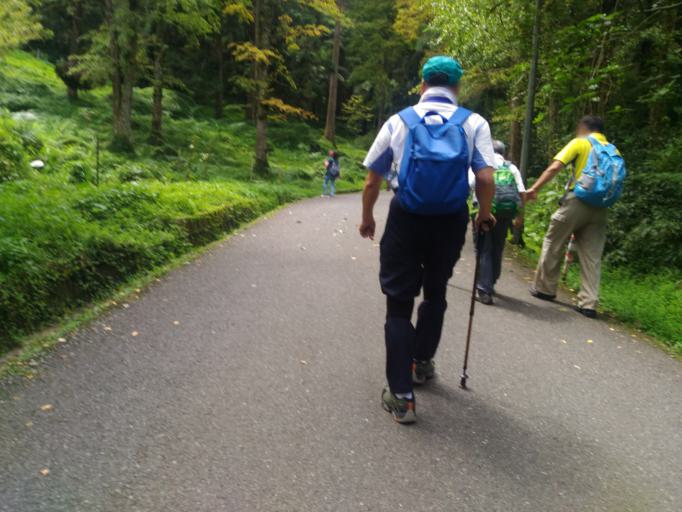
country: TW
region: Taiwan
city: Lugu
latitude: 23.6670
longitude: 120.7984
